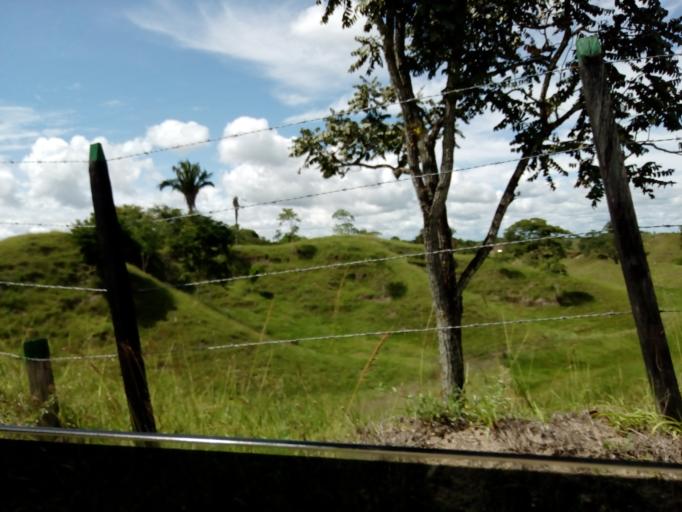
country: CO
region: Boyaca
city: Puerto Boyaca
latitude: 5.9603
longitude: -74.4576
